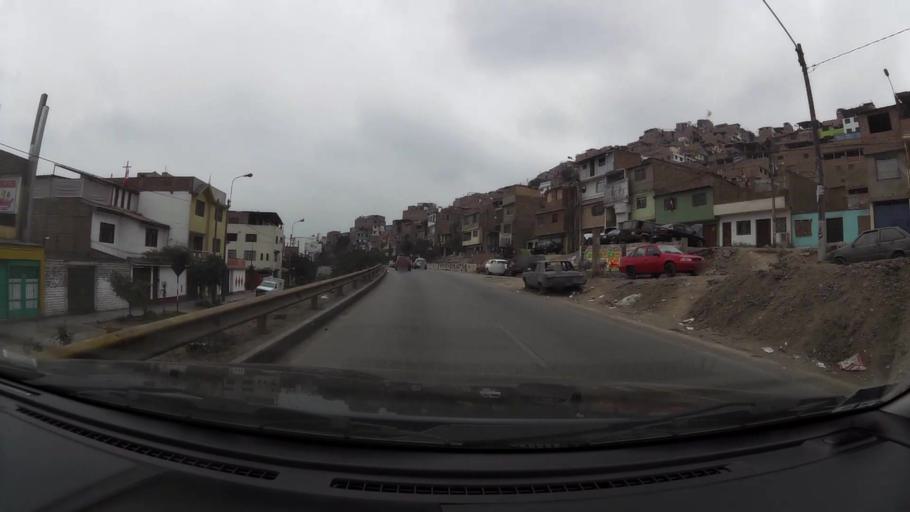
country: PE
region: Lima
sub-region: Lima
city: Surco
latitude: -12.1398
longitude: -76.9748
